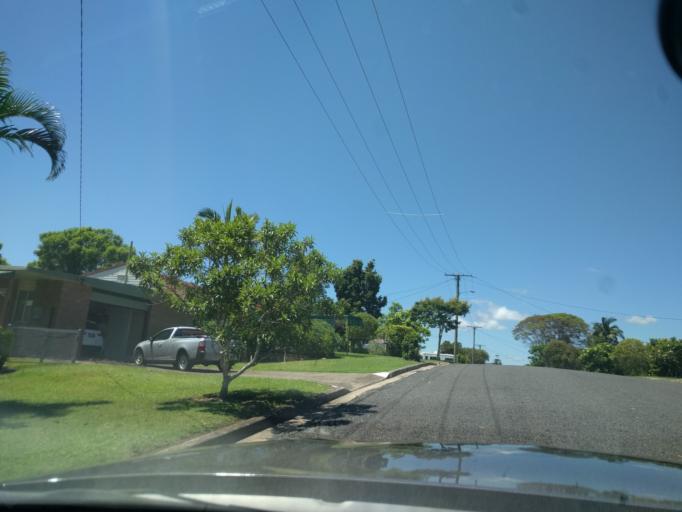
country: AU
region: Queensland
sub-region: Logan
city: Cedar Vale
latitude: -27.9856
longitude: 153.0041
